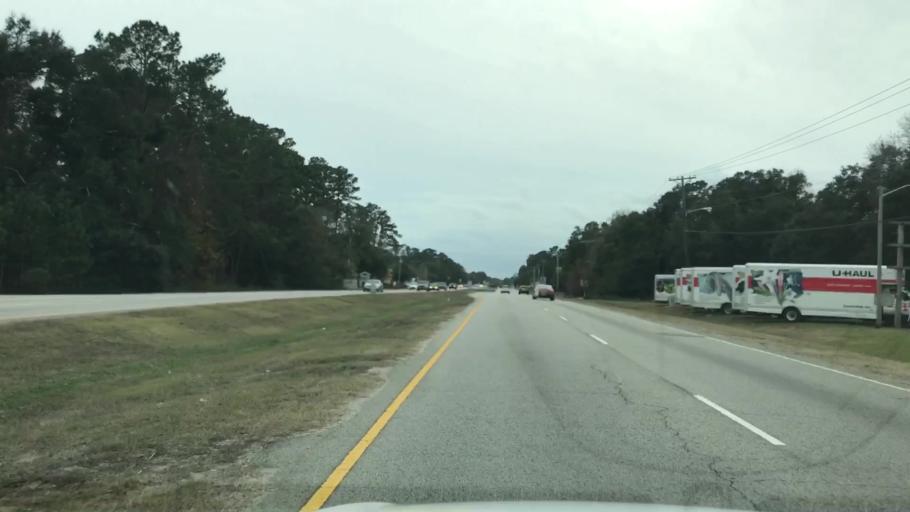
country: US
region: South Carolina
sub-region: Georgetown County
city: Murrells Inlet
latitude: 33.5450
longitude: -79.0517
